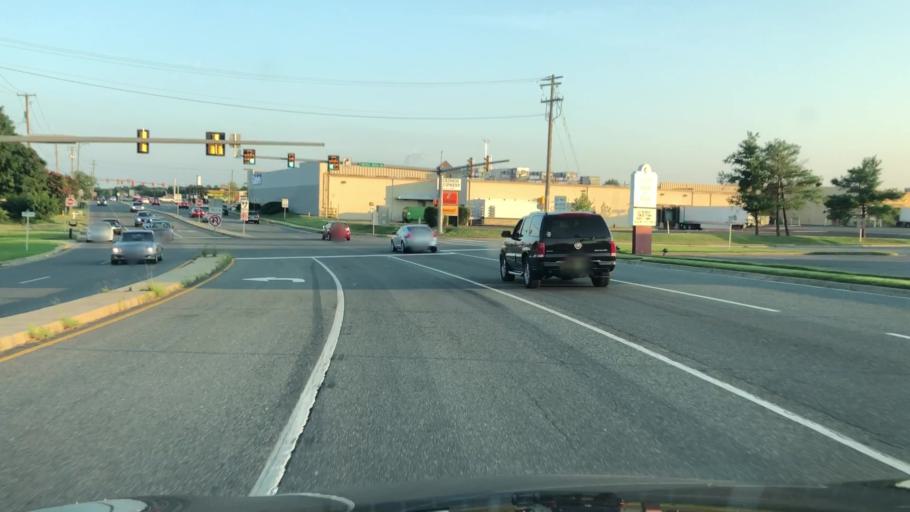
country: US
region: Virginia
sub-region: Stafford County
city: Falmouth
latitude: 38.2967
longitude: -77.5202
